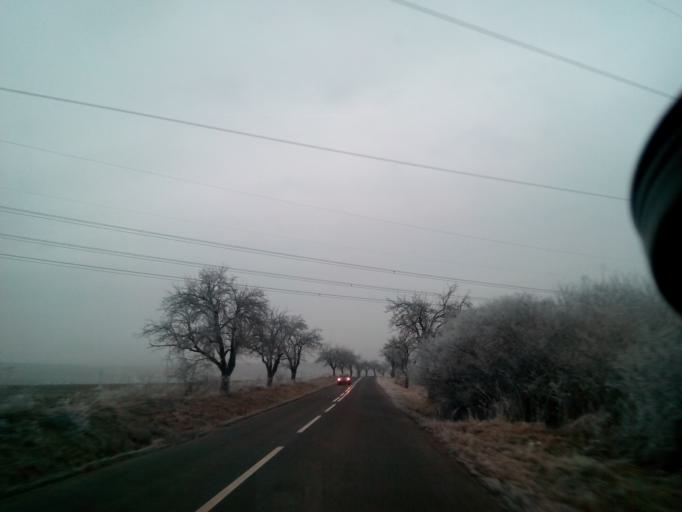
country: SK
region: Presovsky
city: Lubica
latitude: 48.9922
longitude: 20.4401
